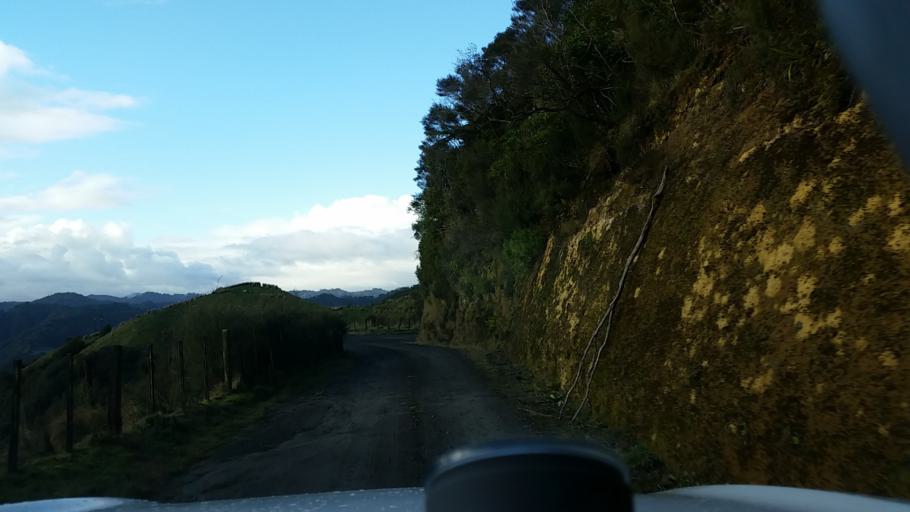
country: NZ
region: Taranaki
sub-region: South Taranaki District
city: Eltham
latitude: -39.4227
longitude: 174.5568
